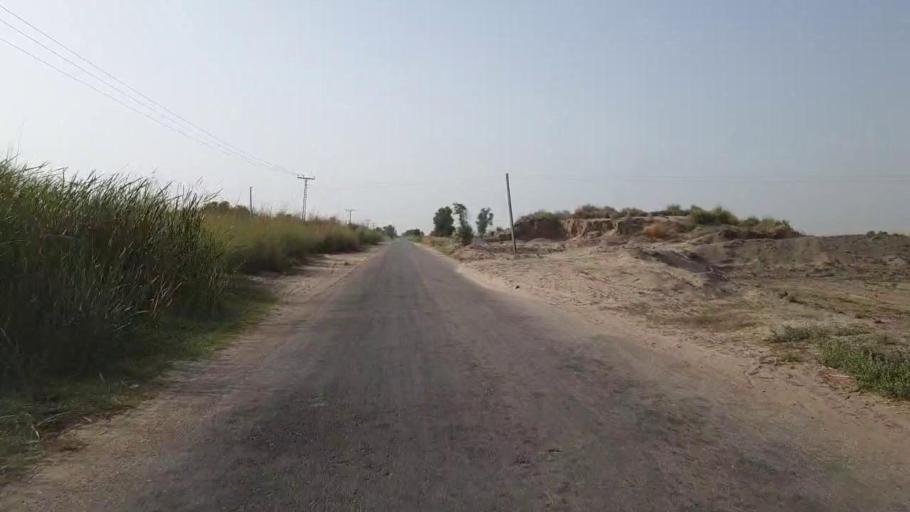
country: PK
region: Sindh
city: Khadro
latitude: 26.3556
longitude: 68.9211
